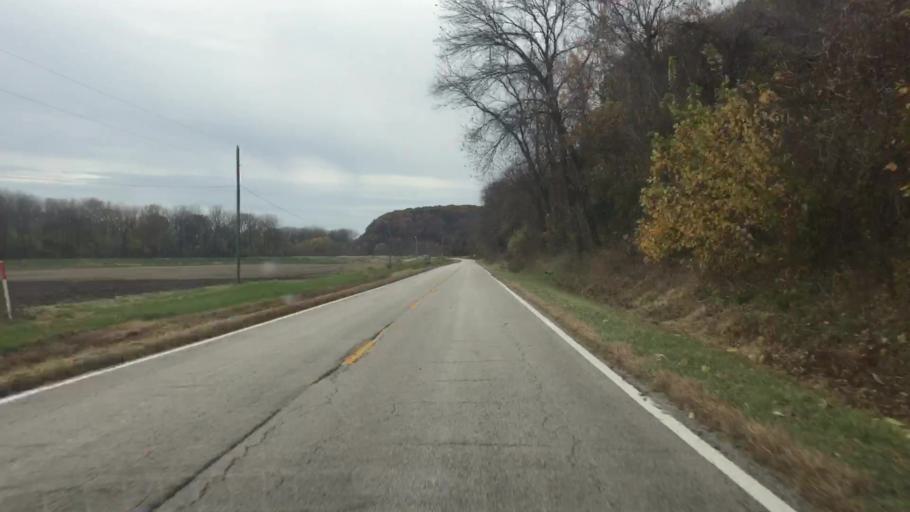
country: US
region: Missouri
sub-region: Gasconade County
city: Hermann
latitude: 38.7045
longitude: -91.6156
